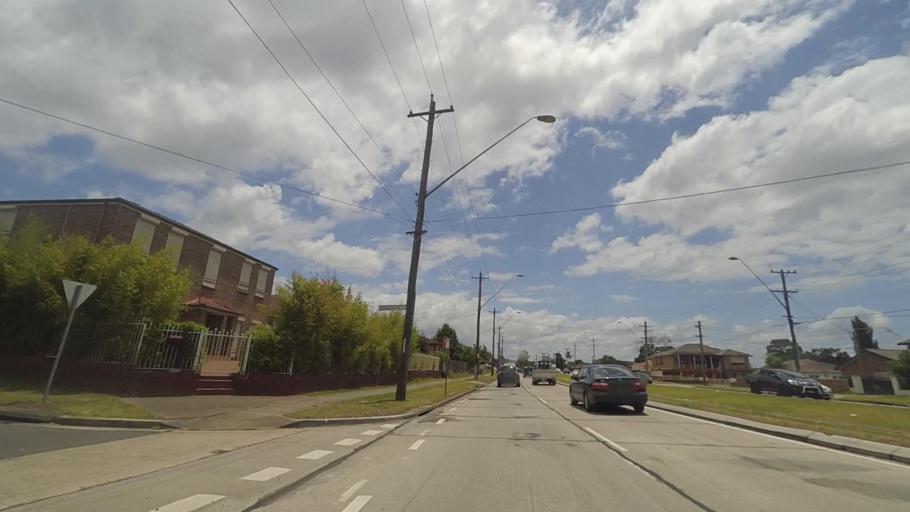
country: AU
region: New South Wales
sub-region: Fairfield
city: Cabramatta West
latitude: -33.8922
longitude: 150.9225
